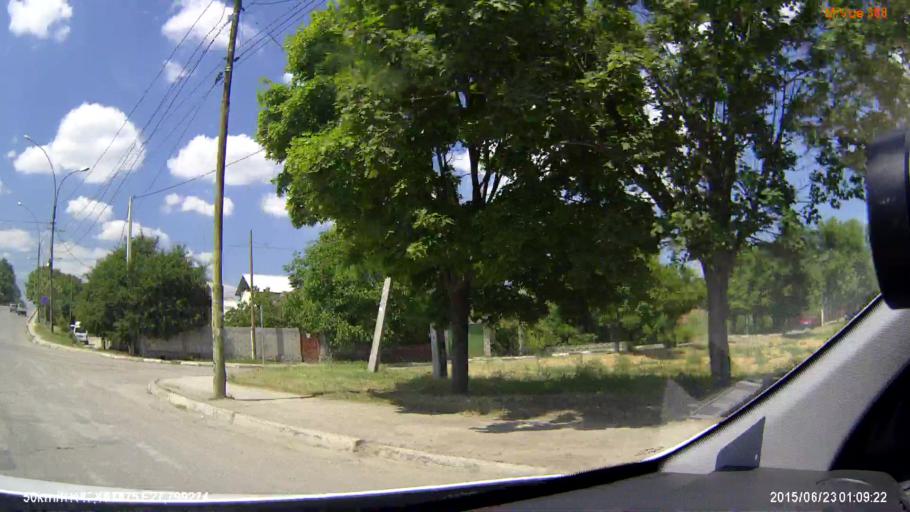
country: MD
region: Ungheni
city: Ungheni
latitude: 47.1978
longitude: 27.7994
